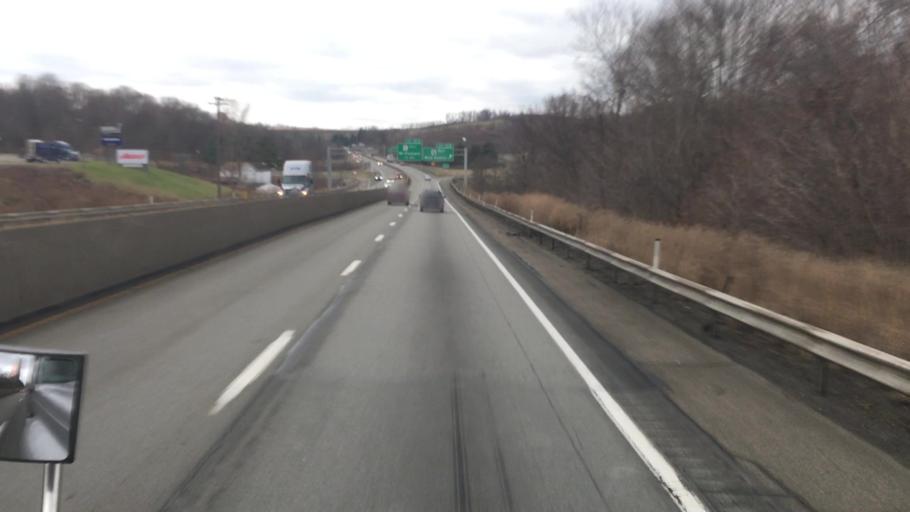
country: US
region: Pennsylvania
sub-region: Westmoreland County
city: West Newton
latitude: 40.1900
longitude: -79.6957
